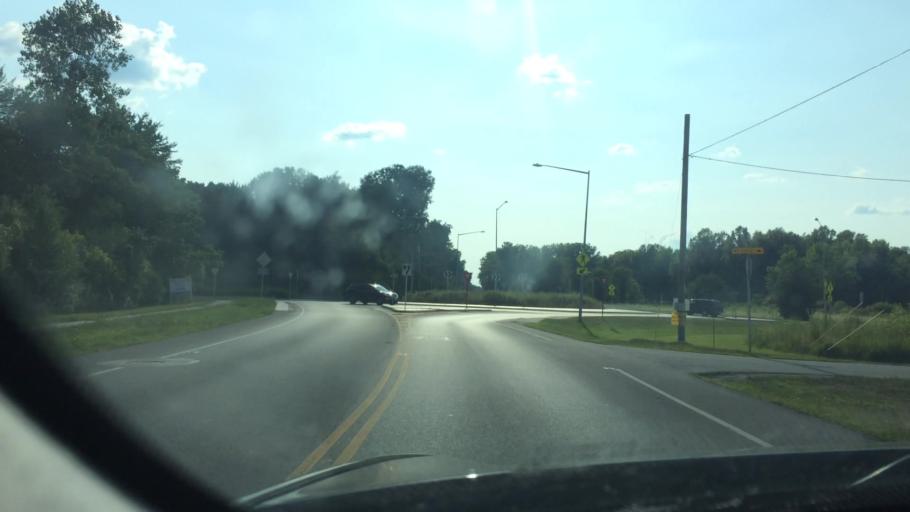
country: US
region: Ohio
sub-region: Lucas County
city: Holland
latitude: 41.6538
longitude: -83.7220
